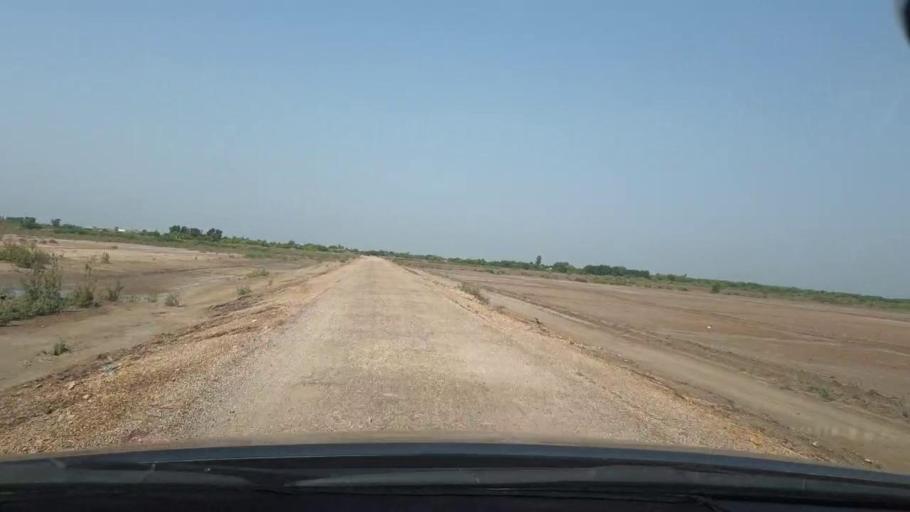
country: PK
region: Sindh
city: Tando Bago
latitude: 24.7179
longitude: 69.1080
